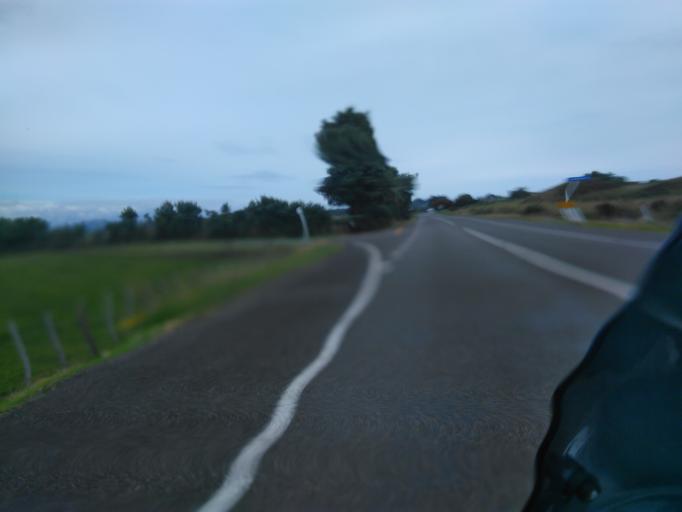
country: NZ
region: Bay of Plenty
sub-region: Opotiki District
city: Opotiki
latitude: -37.9870
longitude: 177.3650
